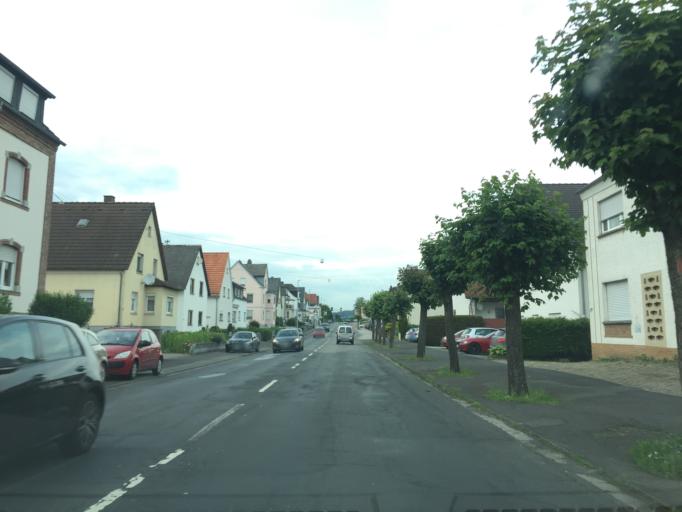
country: DE
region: Hesse
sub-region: Regierungsbezirk Giessen
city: Elz
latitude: 50.4406
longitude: 8.0391
